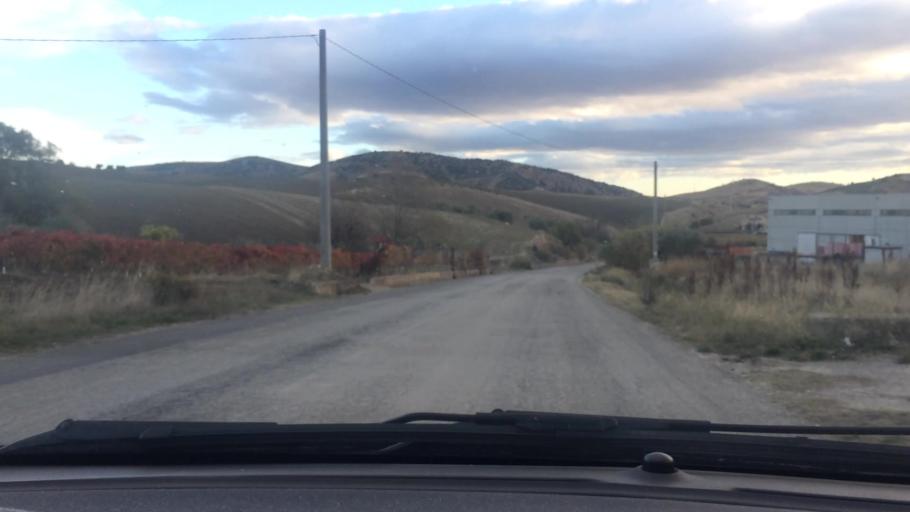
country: IT
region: Basilicate
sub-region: Provincia di Potenza
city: Tolve
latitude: 40.7137
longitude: 16.0224
